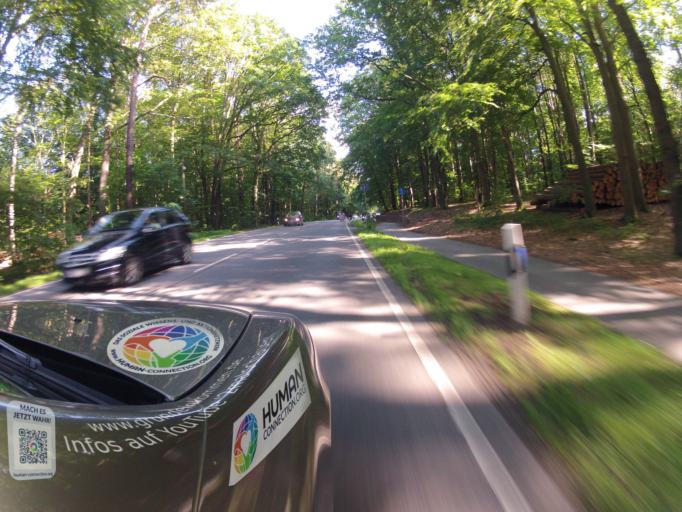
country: DE
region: Mecklenburg-Vorpommern
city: Loddin
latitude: 54.0060
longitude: 14.0589
